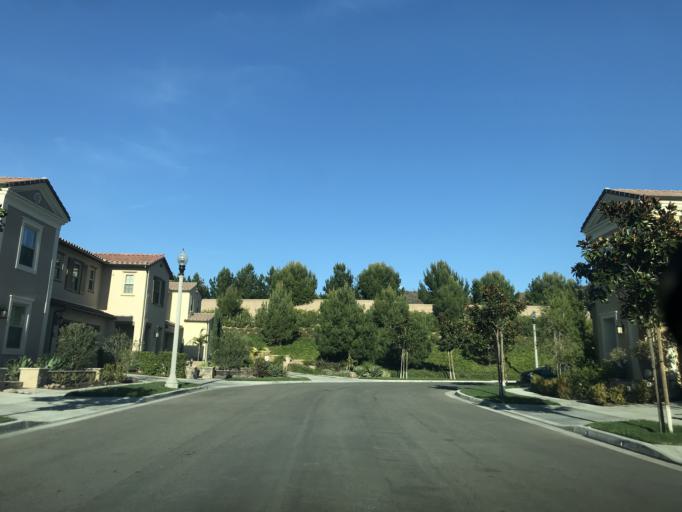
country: US
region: California
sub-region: Orange County
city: North Tustin
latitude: 33.7102
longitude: -117.7379
